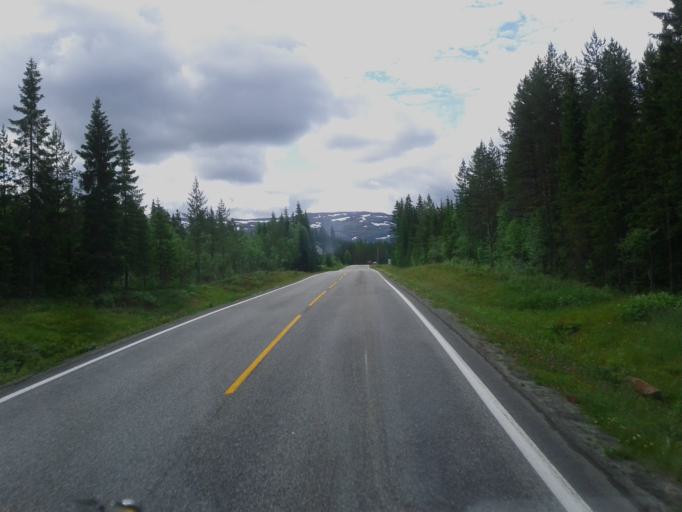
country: NO
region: Nord-Trondelag
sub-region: Hoylandet
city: Hoylandet
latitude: 64.6576
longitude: 12.6488
